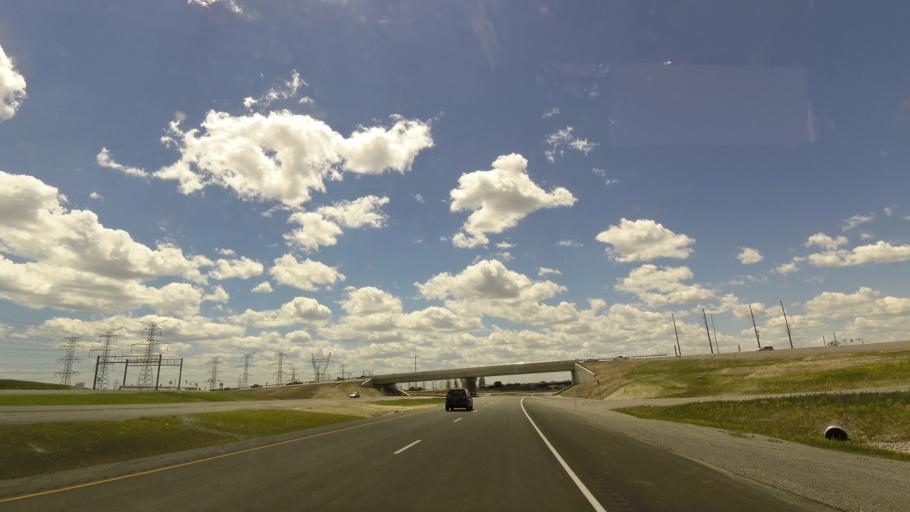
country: CA
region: Ontario
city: Oshawa
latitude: 43.9521
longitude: -78.9389
